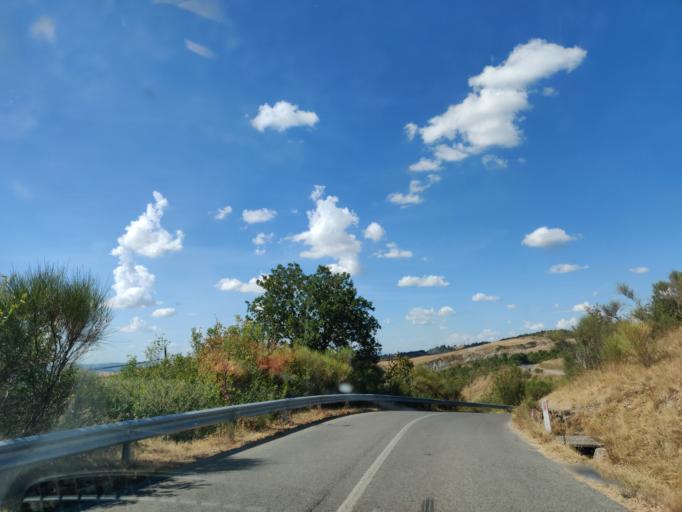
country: IT
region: Tuscany
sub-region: Provincia di Siena
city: Radicofani
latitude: 42.9376
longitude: 11.7333
